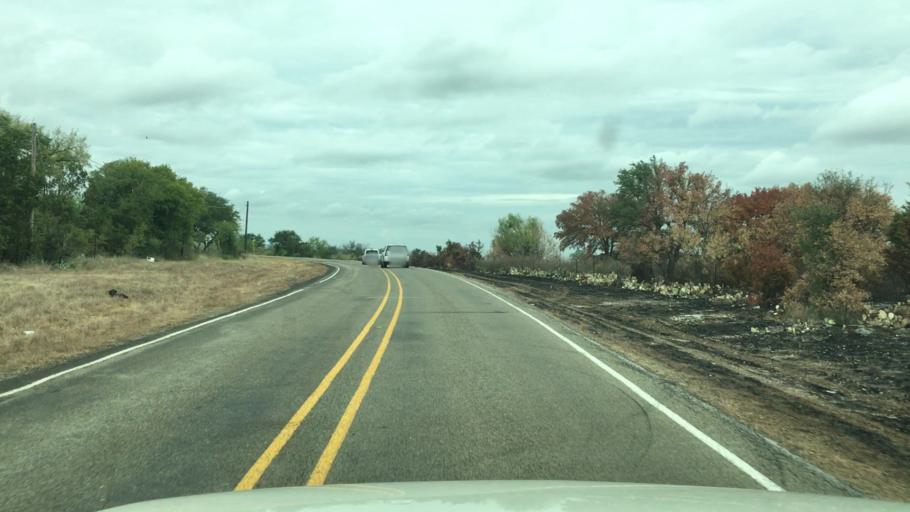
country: US
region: Texas
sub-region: Llano County
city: Horseshoe Bay
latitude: 30.4865
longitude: -98.4313
